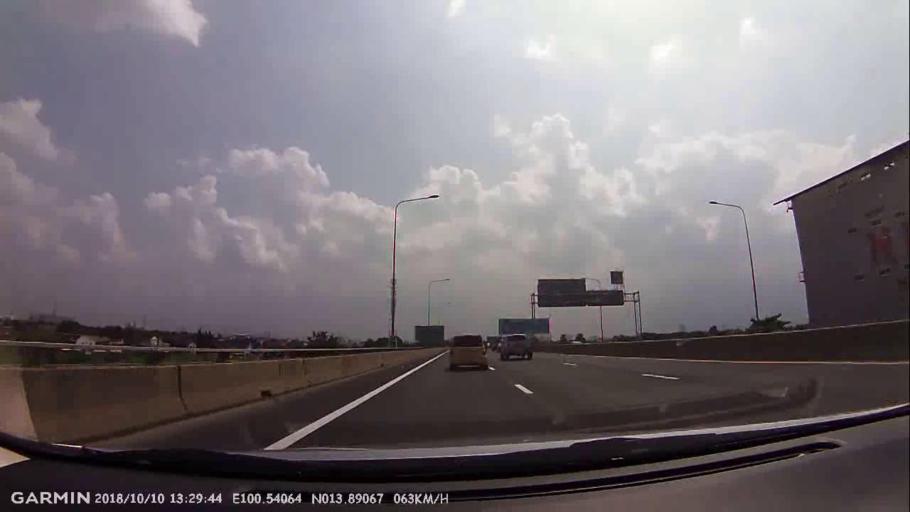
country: TH
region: Bangkok
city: Lak Si
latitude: 13.8905
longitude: 100.5406
